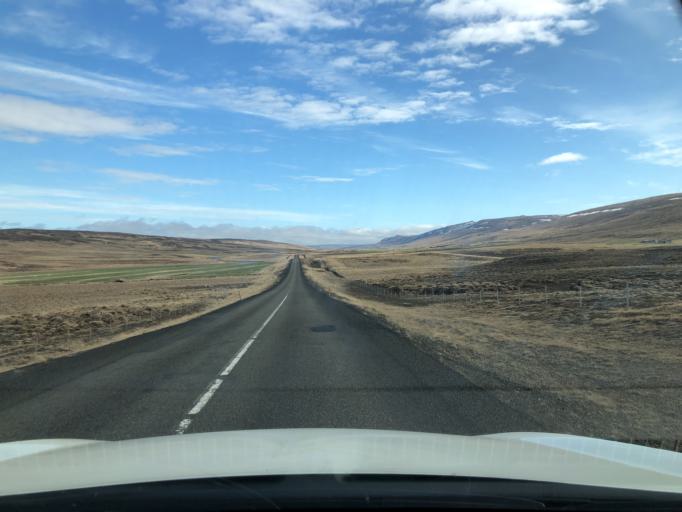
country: IS
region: West
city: Borgarnes
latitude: 65.1151
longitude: -21.6810
